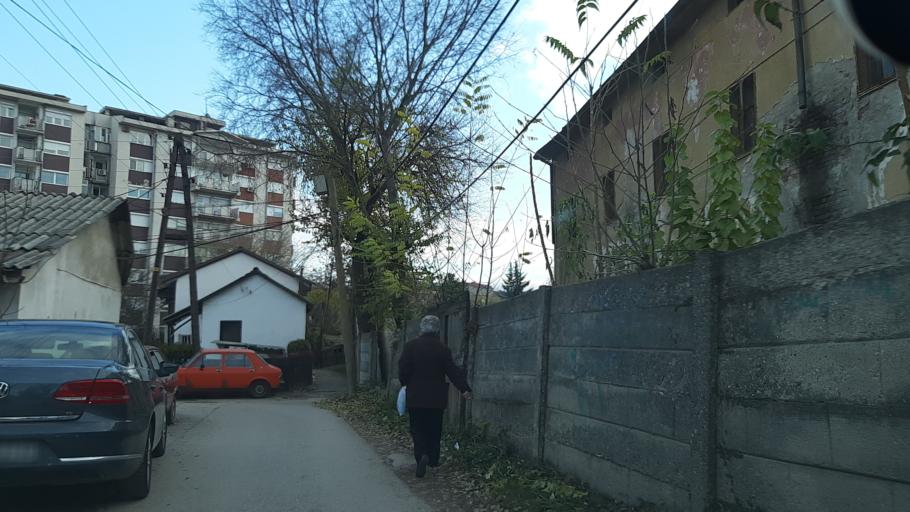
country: MK
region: Karpos
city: Skopje
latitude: 41.9827
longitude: 21.4417
